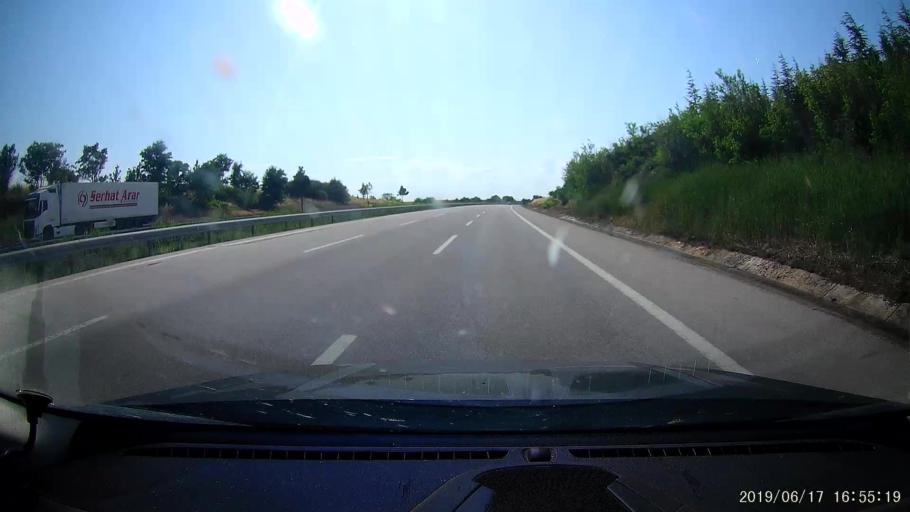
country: TR
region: Edirne
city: Haskoy
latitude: 41.5783
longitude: 26.9692
